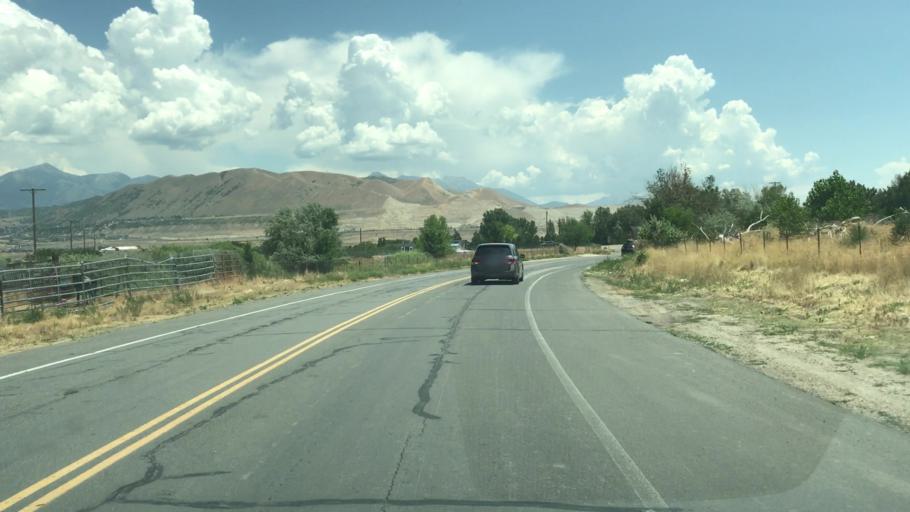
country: US
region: Utah
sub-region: Salt Lake County
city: Bluffdale
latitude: 40.4785
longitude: -111.9480
